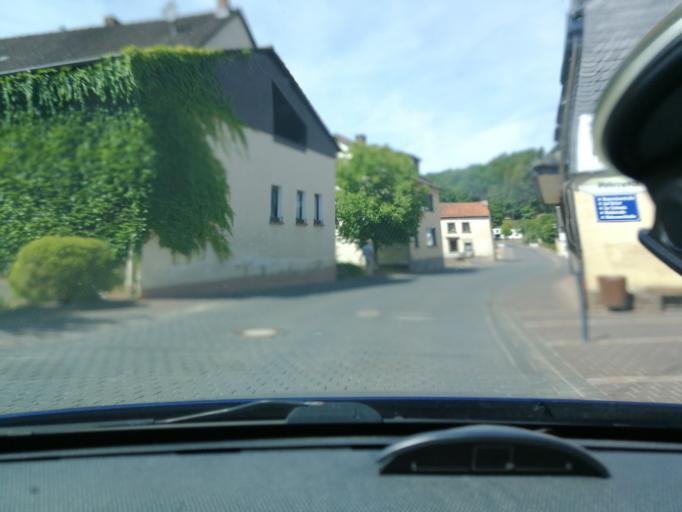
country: DE
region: Rheinland-Pfalz
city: Niersbach
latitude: 49.9405
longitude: 6.7413
